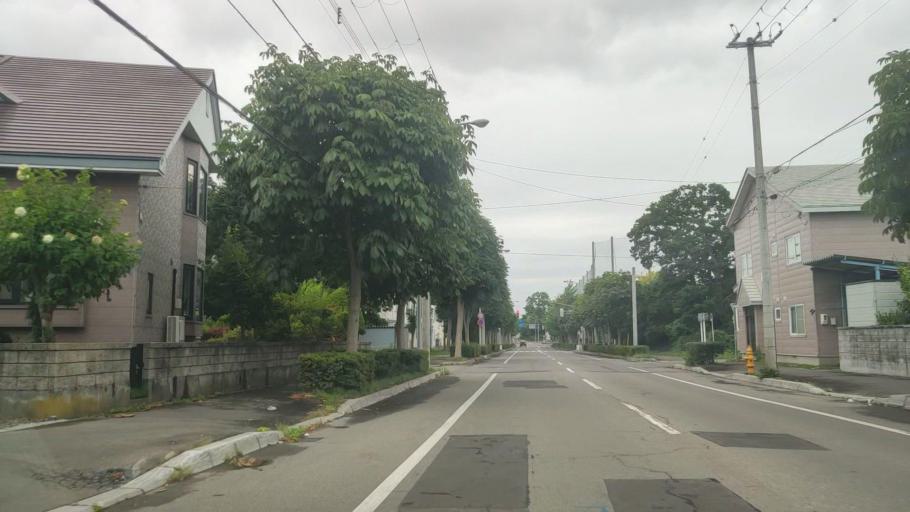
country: JP
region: Hokkaido
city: Hakodate
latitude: 41.7958
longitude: 140.7615
